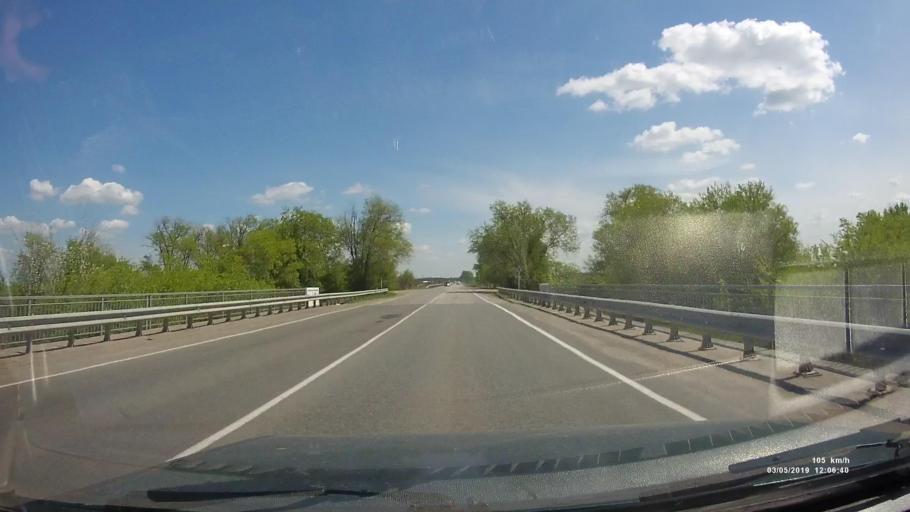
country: RU
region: Rostov
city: Bagayevskaya
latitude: 47.2855
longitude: 40.4572
